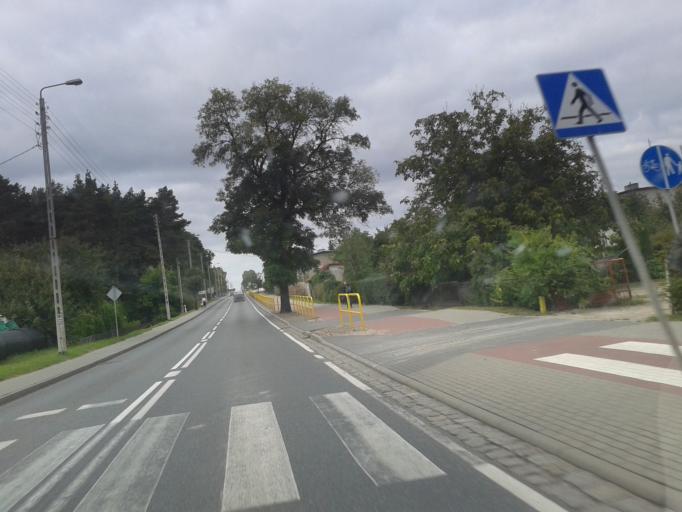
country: PL
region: Kujawsko-Pomorskie
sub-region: Powiat sepolenski
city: Sepolno Krajenskie
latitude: 53.4590
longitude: 17.5325
